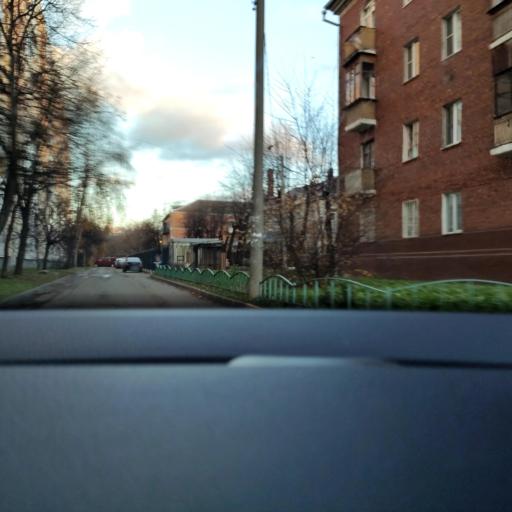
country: RU
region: Moskovskaya
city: Vidnoye
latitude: 55.5547
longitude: 37.6936
